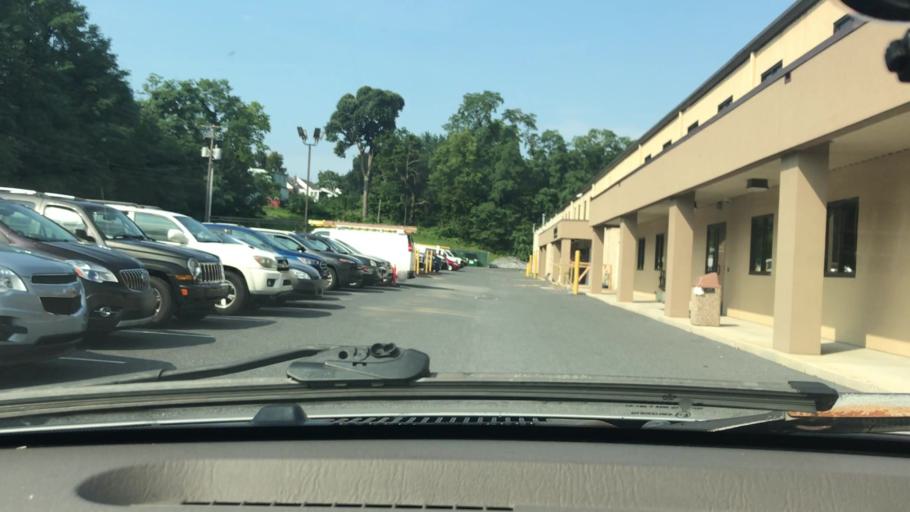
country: US
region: Pennsylvania
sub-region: Dauphin County
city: Linglestown
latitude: 40.3234
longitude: -76.7814
